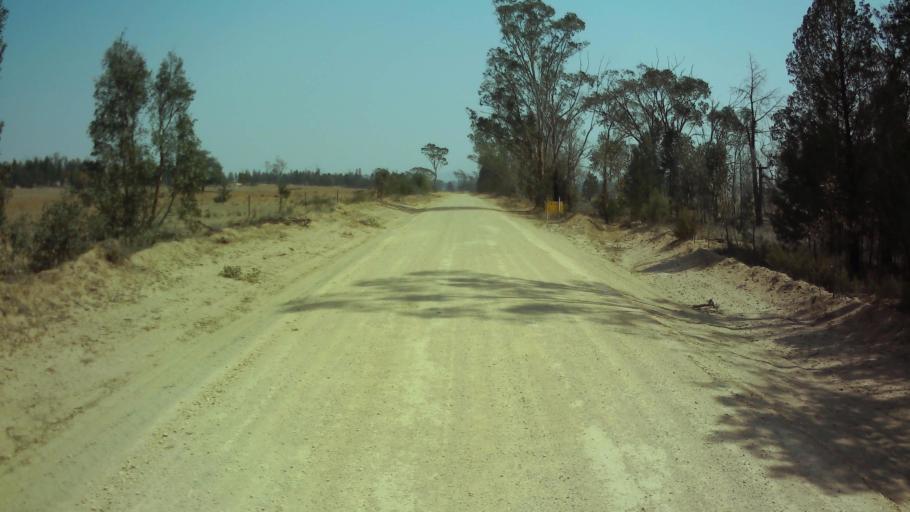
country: AU
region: New South Wales
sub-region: Weddin
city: Grenfell
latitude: -33.6553
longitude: 148.2730
